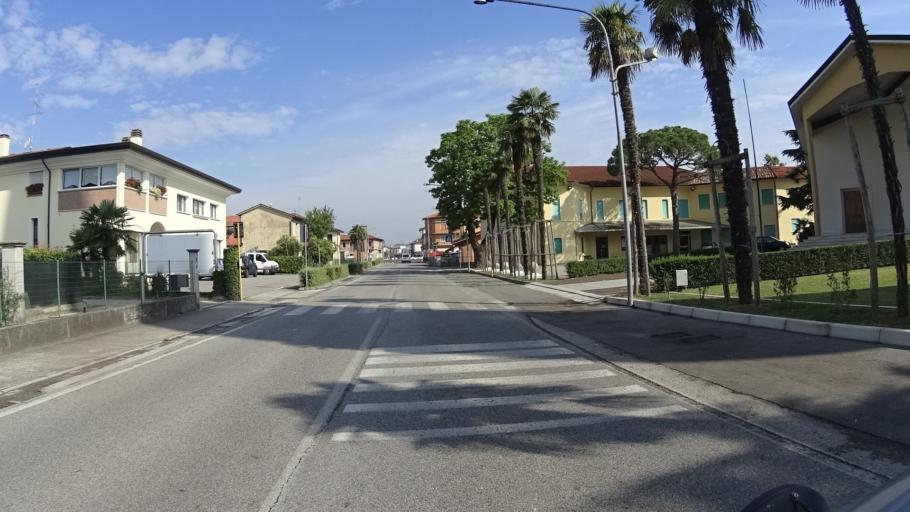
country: IT
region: Veneto
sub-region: Provincia di Venezia
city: Lugugnana
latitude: 45.7319
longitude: 12.9574
